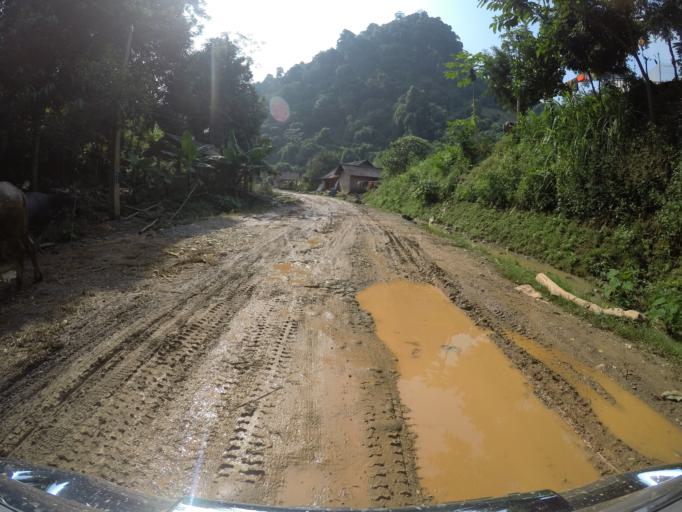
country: VN
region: Yen Bai
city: Co Phuc
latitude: 21.7940
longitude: 104.6411
